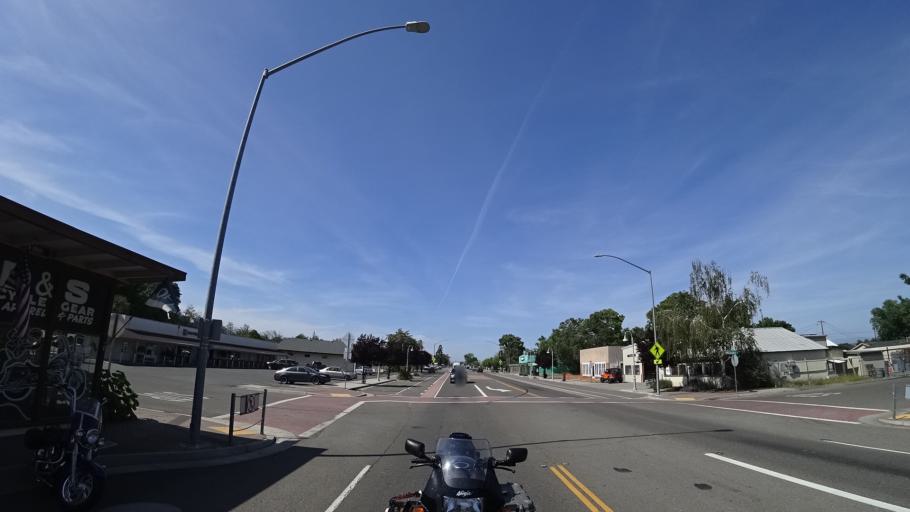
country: US
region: California
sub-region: Tehama County
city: Los Molinos
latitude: 40.0239
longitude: -122.0999
